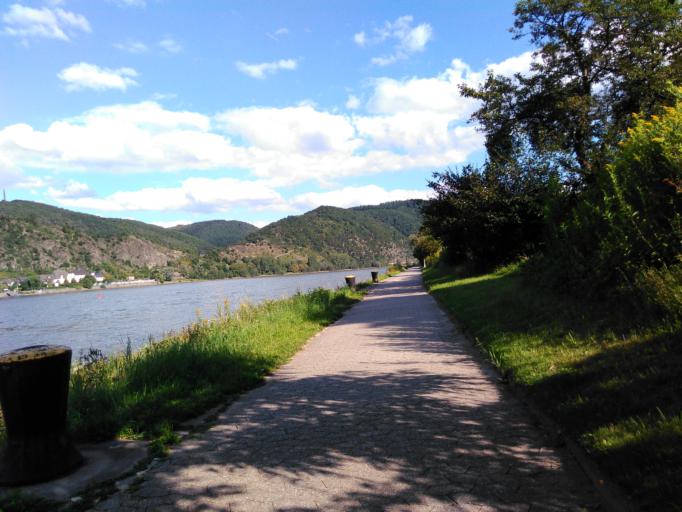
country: DE
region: Rheinland-Pfalz
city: Brey
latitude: 50.2715
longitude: 7.6369
